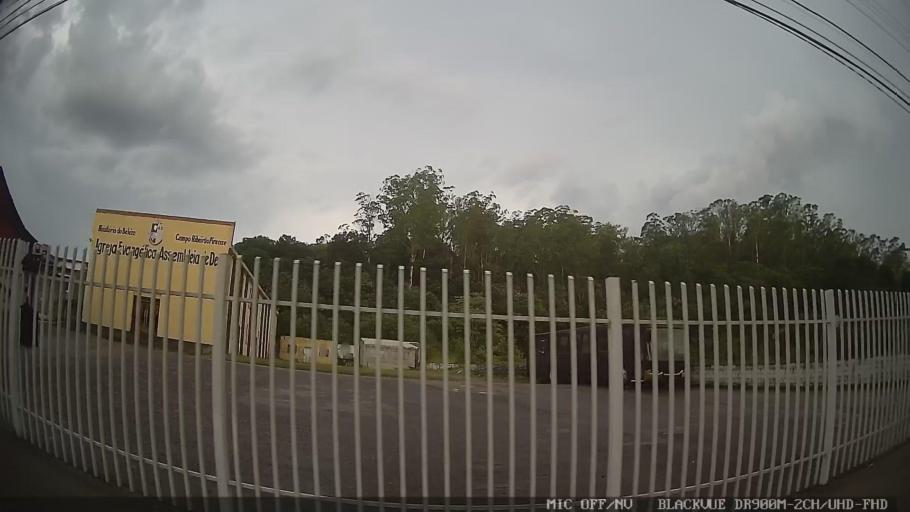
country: BR
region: Sao Paulo
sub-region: Ribeirao Pires
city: Ribeirao Pires
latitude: -23.7051
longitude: -46.4054
